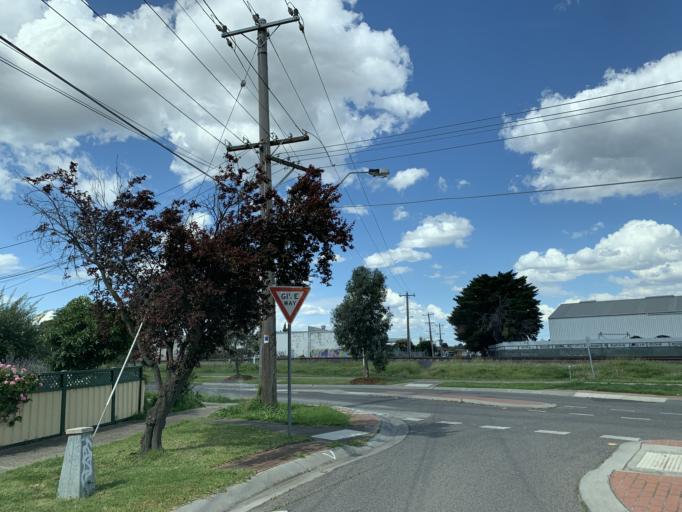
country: AU
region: Victoria
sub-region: Brimbank
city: Sunshine North
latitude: -37.7656
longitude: 144.8286
